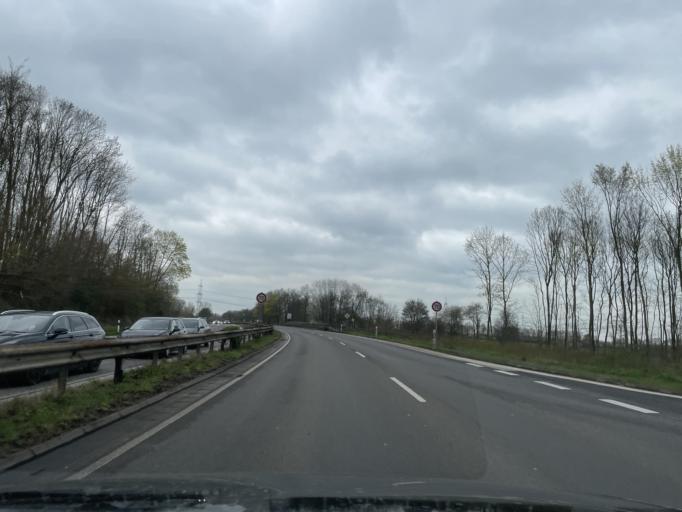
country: DE
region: North Rhine-Westphalia
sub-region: Regierungsbezirk Dusseldorf
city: Monchengladbach
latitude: 51.2234
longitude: 6.4347
